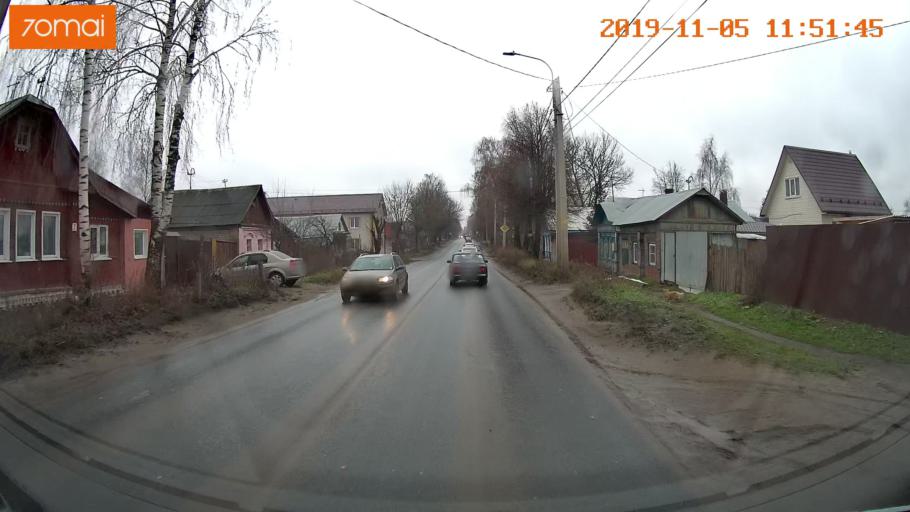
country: RU
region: Ivanovo
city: Bogorodskoye
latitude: 57.0039
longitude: 41.0287
